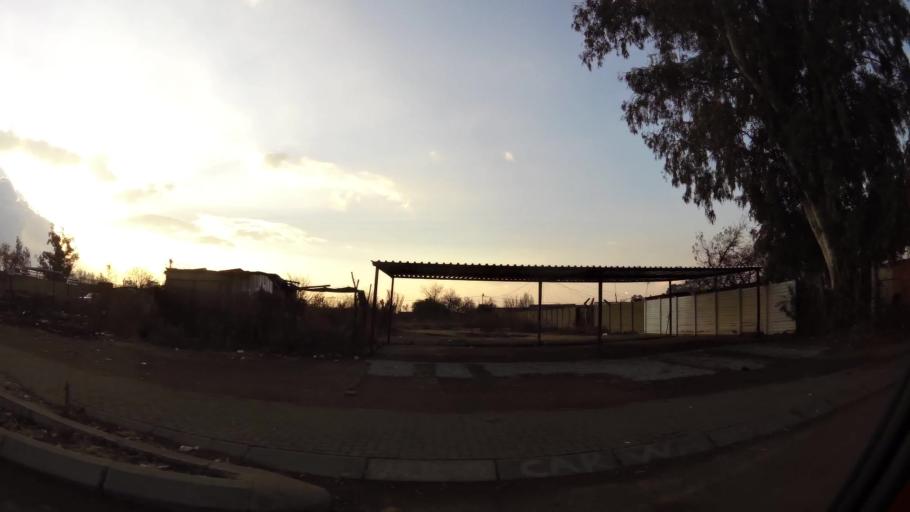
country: ZA
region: Gauteng
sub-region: City of Johannesburg Metropolitan Municipality
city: Orange Farm
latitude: -26.5362
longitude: 27.8377
